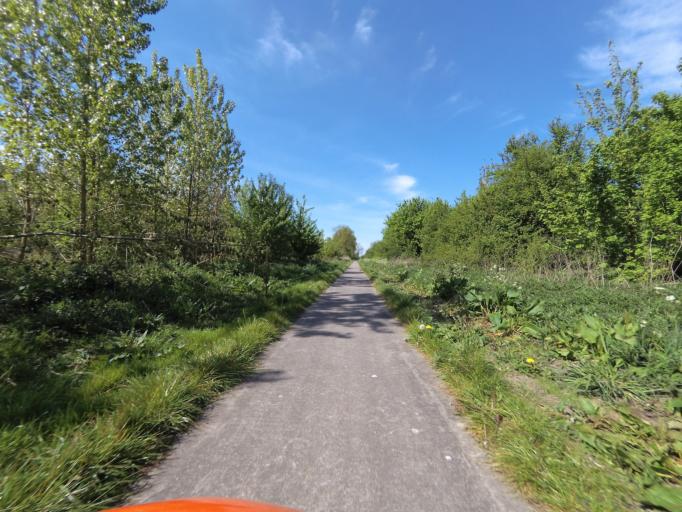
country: NL
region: Flevoland
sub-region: Gemeente Dronten
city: Dronten
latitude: 52.5206
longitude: 5.6686
